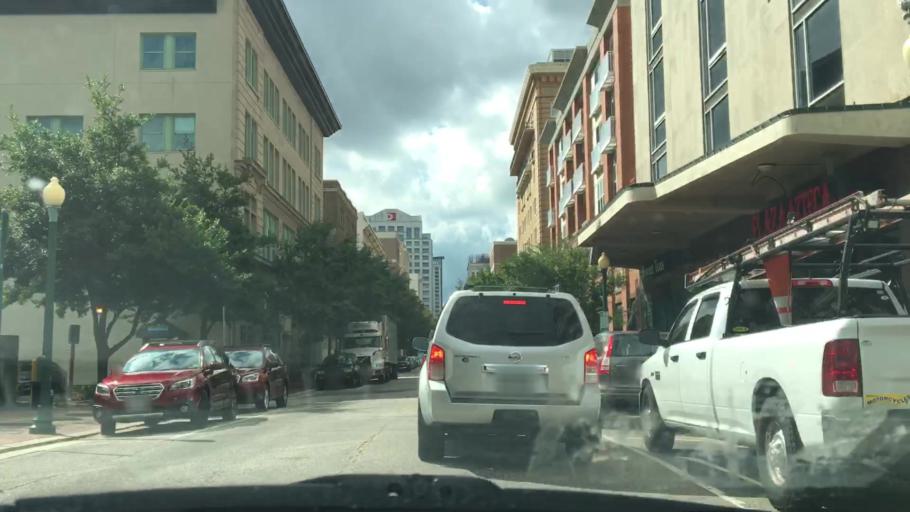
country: US
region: Virginia
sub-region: City of Norfolk
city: Norfolk
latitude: 36.8519
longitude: -76.2895
